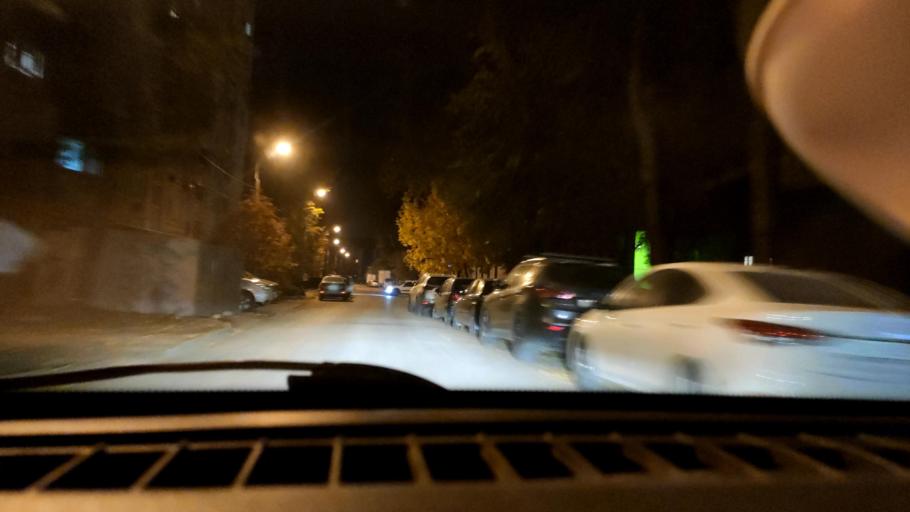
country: RU
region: Samara
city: Samara
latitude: 53.2217
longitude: 50.2525
